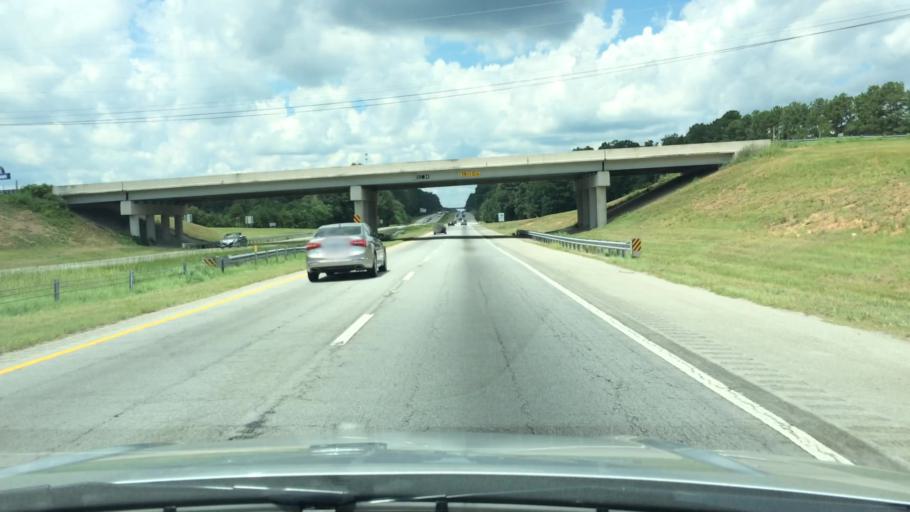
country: US
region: South Carolina
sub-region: Newberry County
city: Newberry
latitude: 34.3107
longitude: -81.5735
